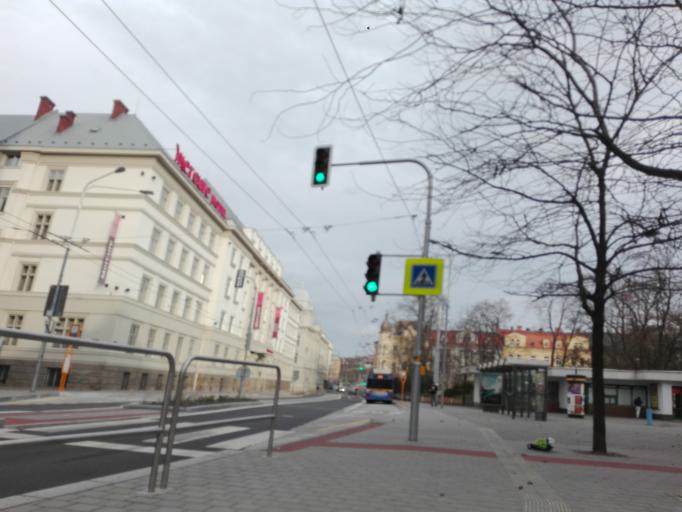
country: CZ
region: Moravskoslezsky
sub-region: Okres Ostrava-Mesto
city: Ostrava
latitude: 49.8384
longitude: 18.2872
